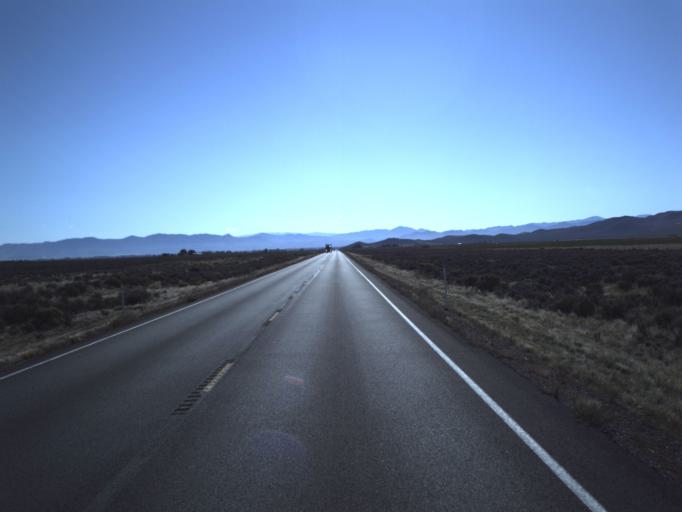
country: US
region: Utah
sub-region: Washington County
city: Enterprise
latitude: 37.7641
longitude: -113.8107
